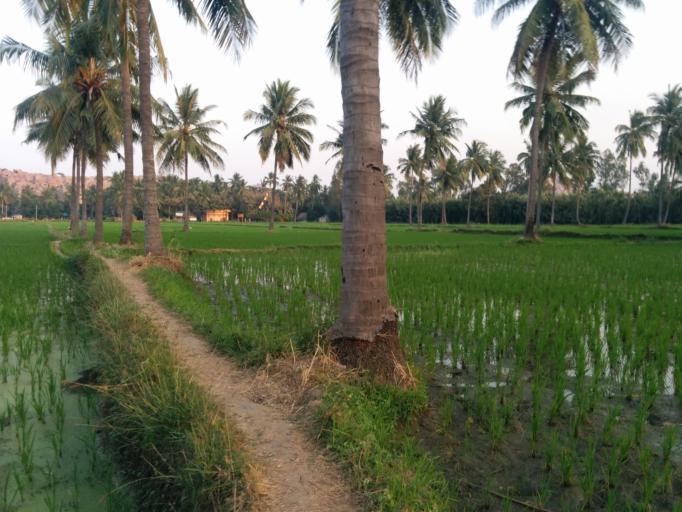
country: IN
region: Karnataka
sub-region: Bellary
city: Hampi
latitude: 15.3404
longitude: 76.4590
